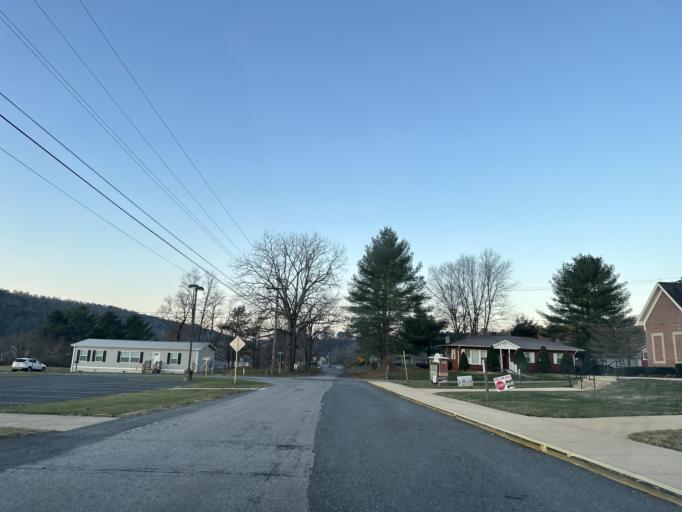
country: US
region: Virginia
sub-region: Rockbridge County
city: East Lexington
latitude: 38.0817
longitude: -79.3804
